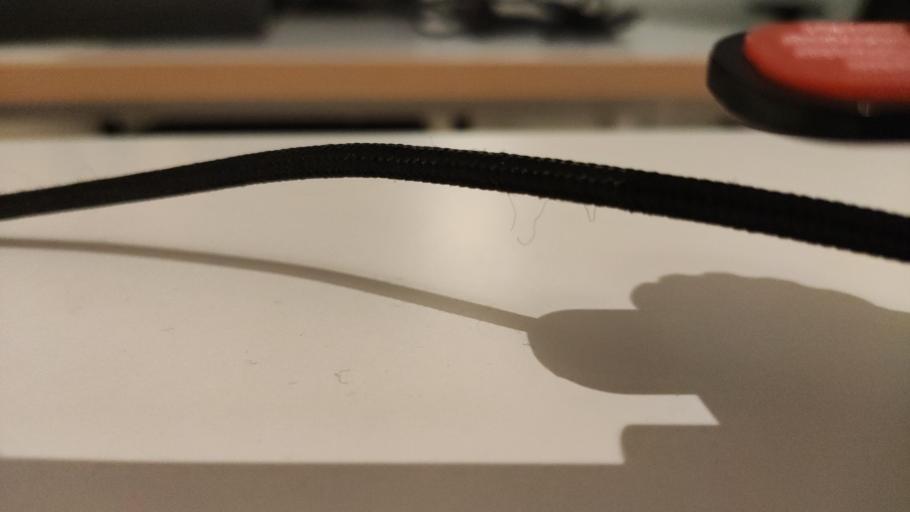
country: RU
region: Moskovskaya
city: Il'inskiy Pogost
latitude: 55.5123
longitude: 38.8714
